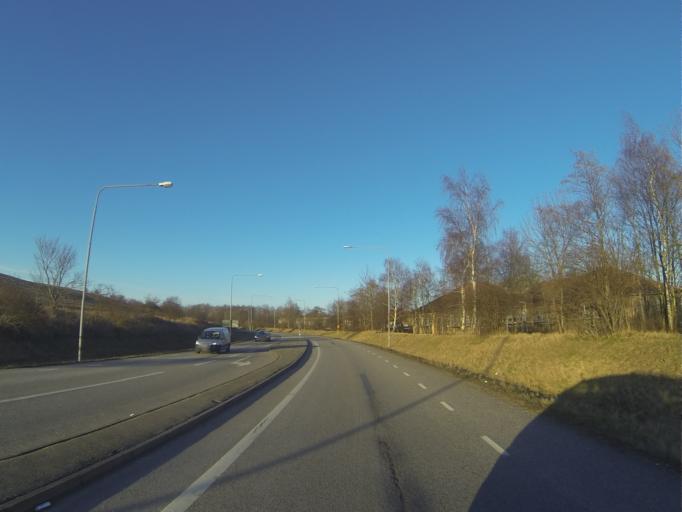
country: SE
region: Skane
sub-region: Malmo
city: Oxie
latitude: 55.5394
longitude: 13.0919
